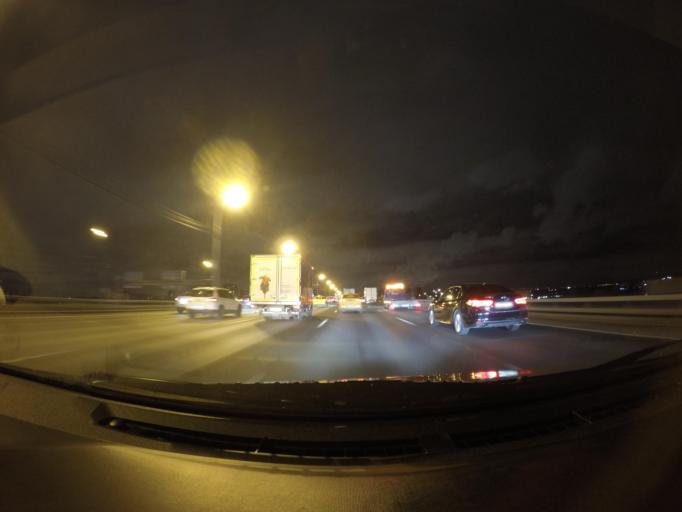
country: RU
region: Moskovskaya
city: Alekseyevka
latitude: 55.6218
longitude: 37.7906
